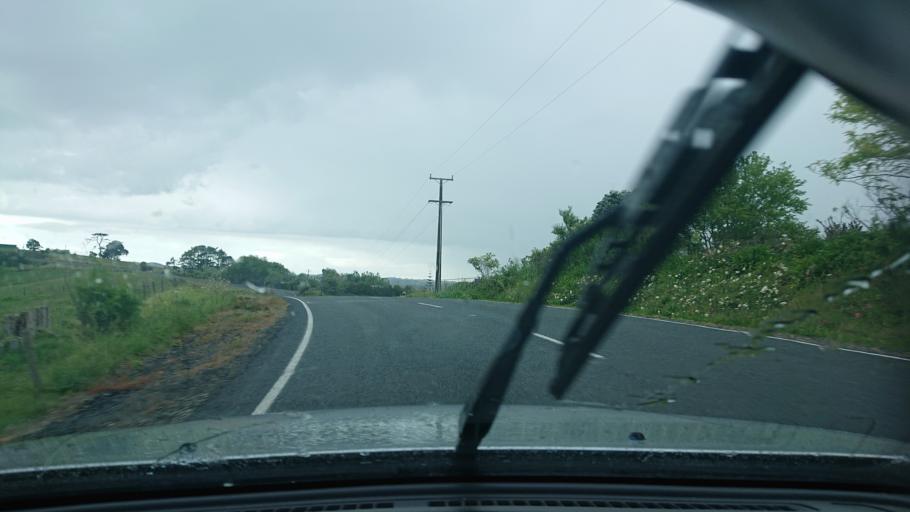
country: NZ
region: Auckland
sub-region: Auckland
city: Wellsford
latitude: -36.3351
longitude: 174.3948
